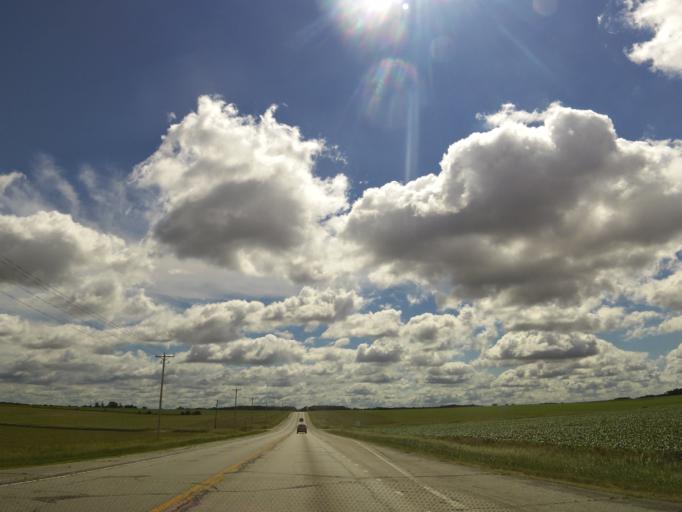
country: US
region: Minnesota
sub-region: Fillmore County
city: Spring Valley
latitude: 43.7106
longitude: -92.4713
